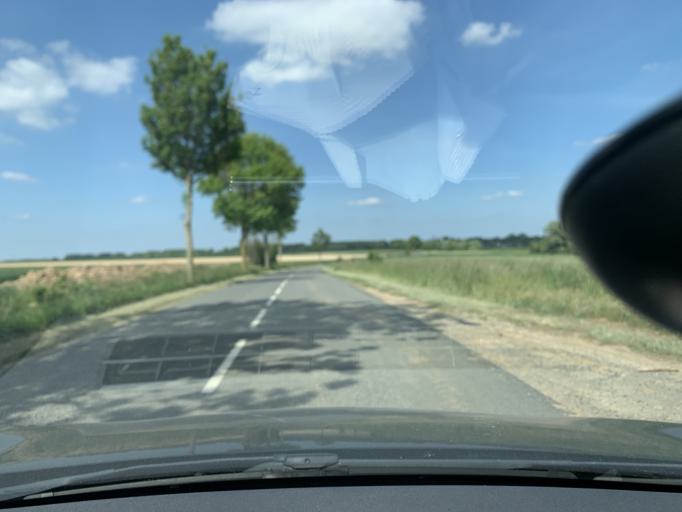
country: FR
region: Nord-Pas-de-Calais
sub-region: Departement du Pas-de-Calais
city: Marquion
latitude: 50.2285
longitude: 3.0842
